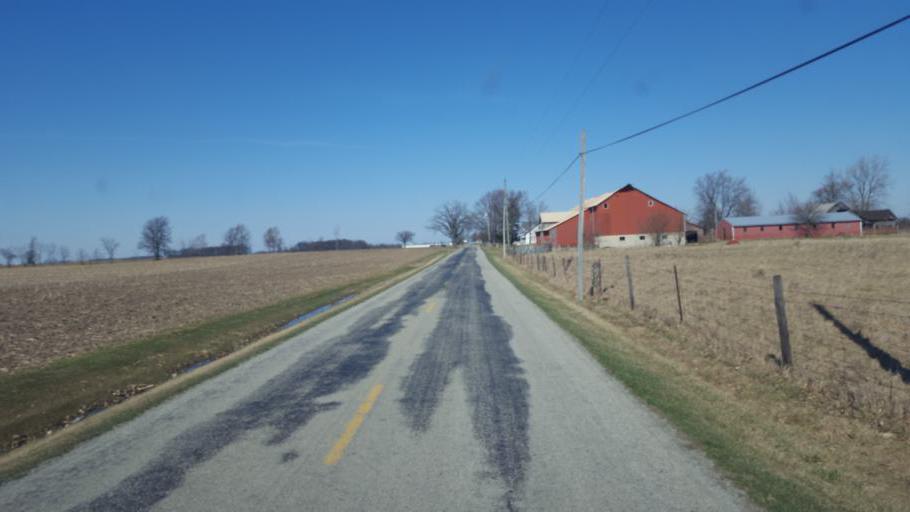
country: US
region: Ohio
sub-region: Union County
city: Richwood
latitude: 40.5101
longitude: -83.4375
